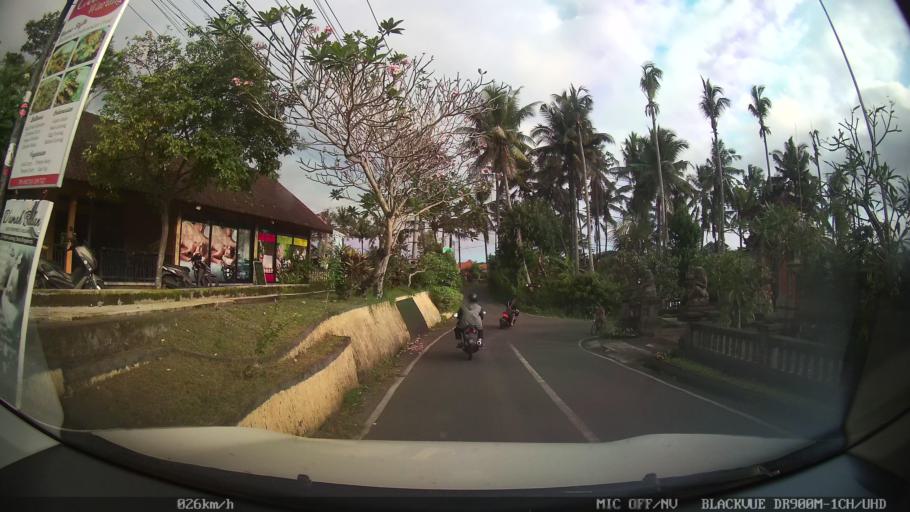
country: ID
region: Bali
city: Banjar Tebongkang
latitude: -8.5209
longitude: 115.2506
